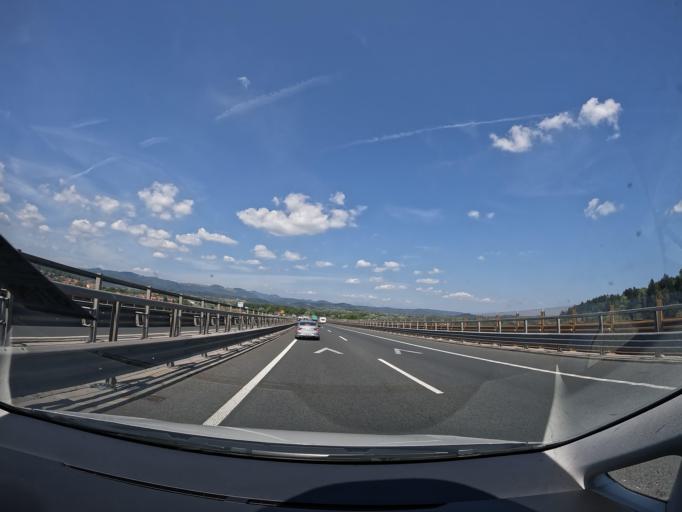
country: SI
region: Vrhnika
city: Verd
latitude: 45.9549
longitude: 14.3051
